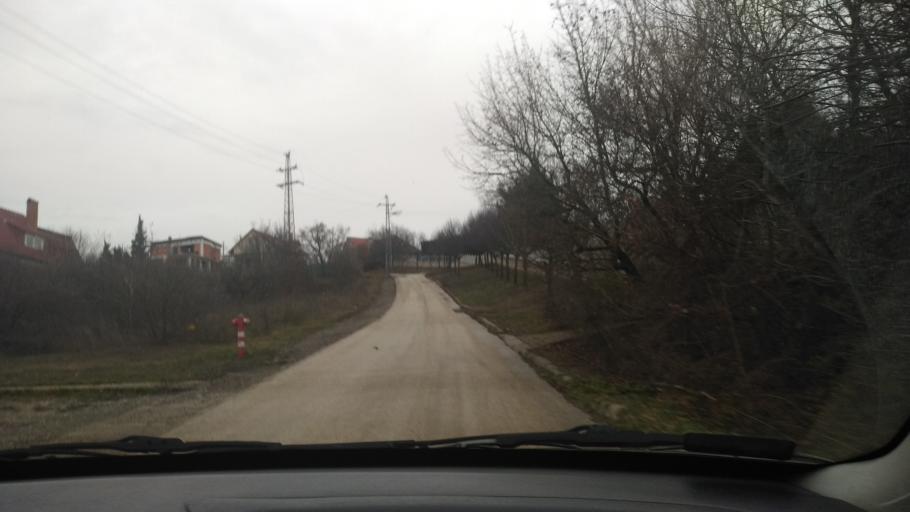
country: HU
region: Pest
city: Szentendre
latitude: 47.6958
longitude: 19.0527
